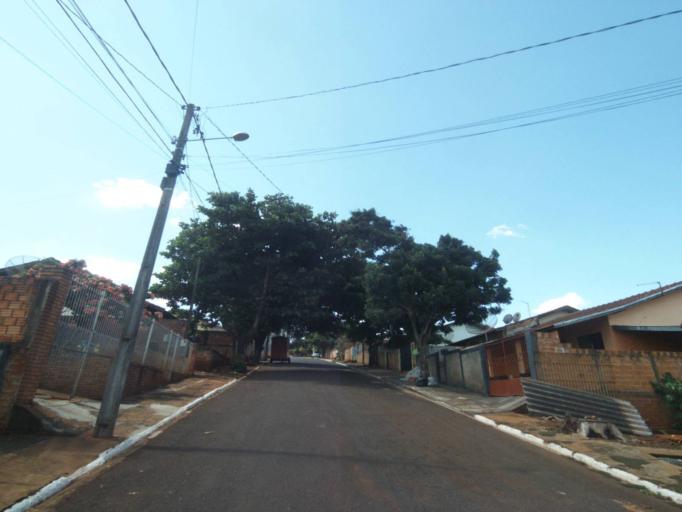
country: BR
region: Parana
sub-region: Sertanopolis
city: Sertanopolis
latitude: -23.0474
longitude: -50.8226
